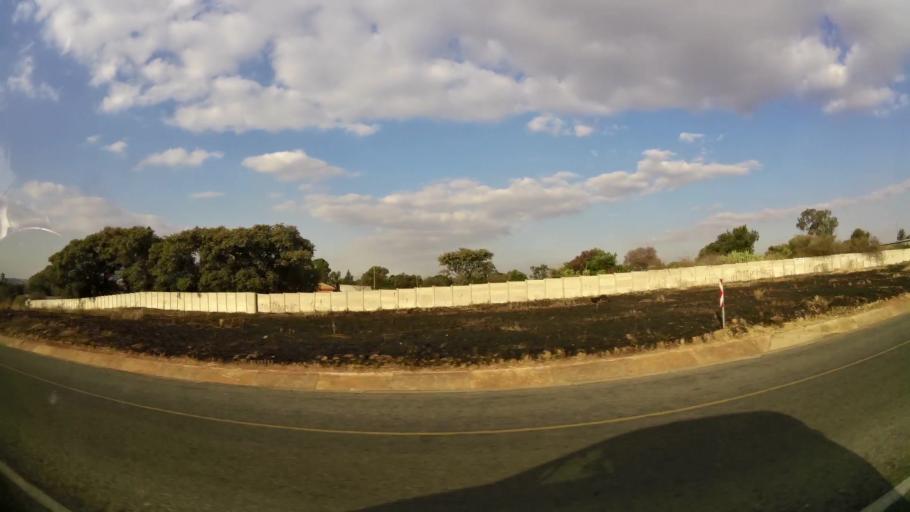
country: ZA
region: Gauteng
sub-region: West Rand District Municipality
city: Krugersdorp
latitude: -26.0928
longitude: 27.7325
